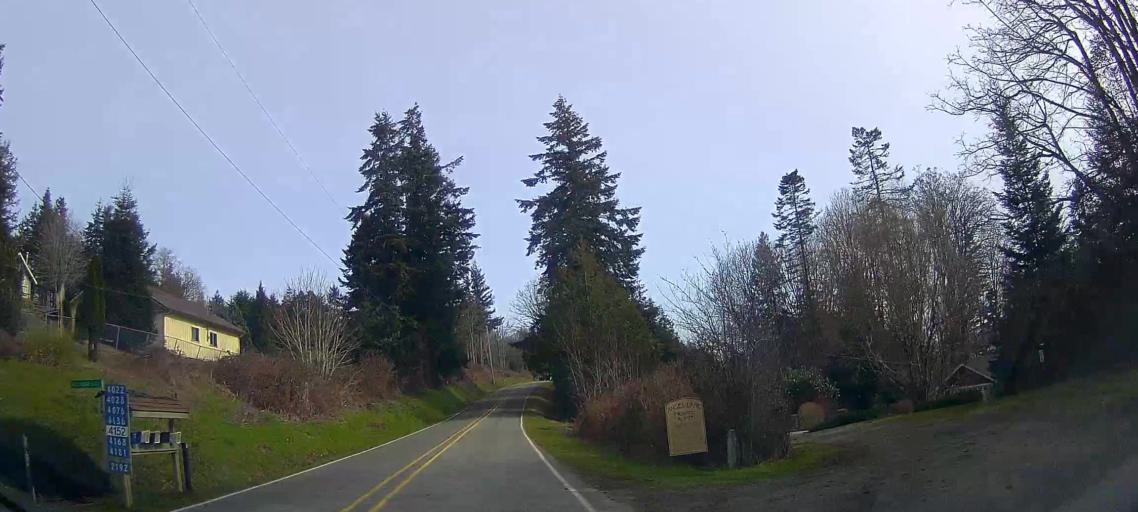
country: US
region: Washington
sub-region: Island County
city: Langley
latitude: 48.0579
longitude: -122.3681
